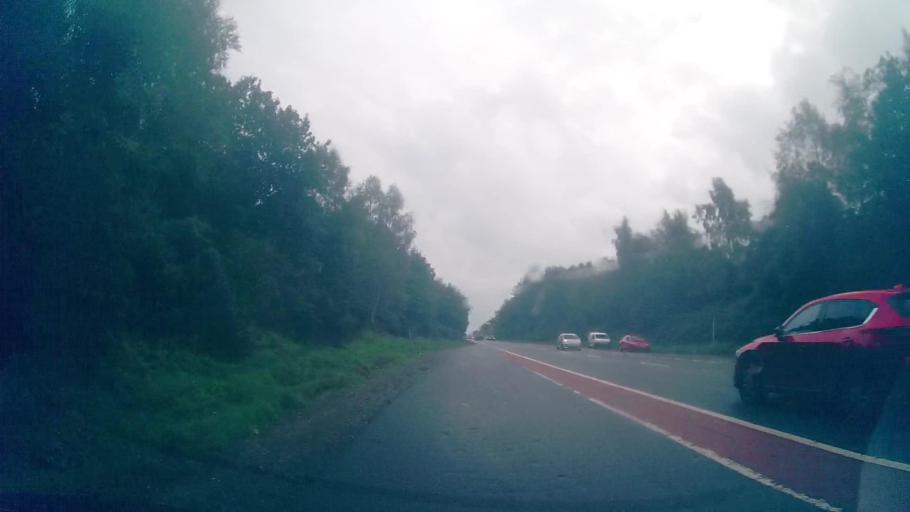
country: GB
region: Scotland
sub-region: Dumfries and Galloway
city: Locharbriggs
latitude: 55.0847
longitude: -3.5897
